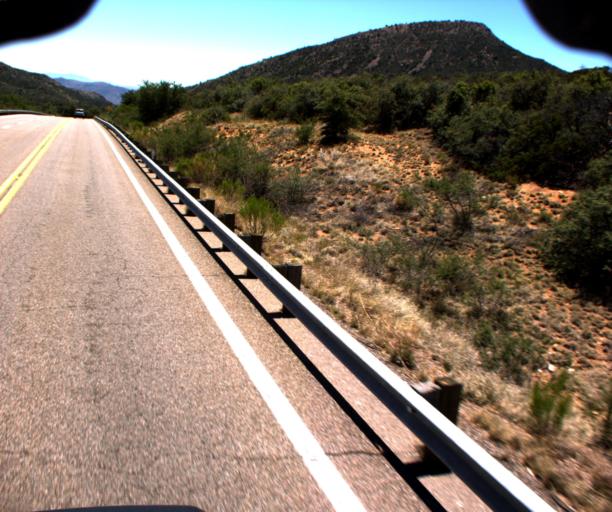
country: US
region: Arizona
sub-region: Gila County
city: Globe
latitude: 33.2362
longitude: -110.7848
